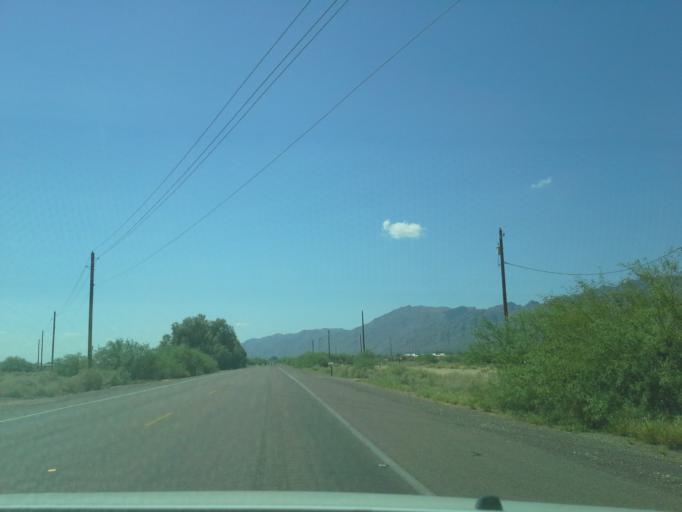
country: US
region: Arizona
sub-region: Maricopa County
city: Laveen
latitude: 33.3000
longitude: -112.1691
